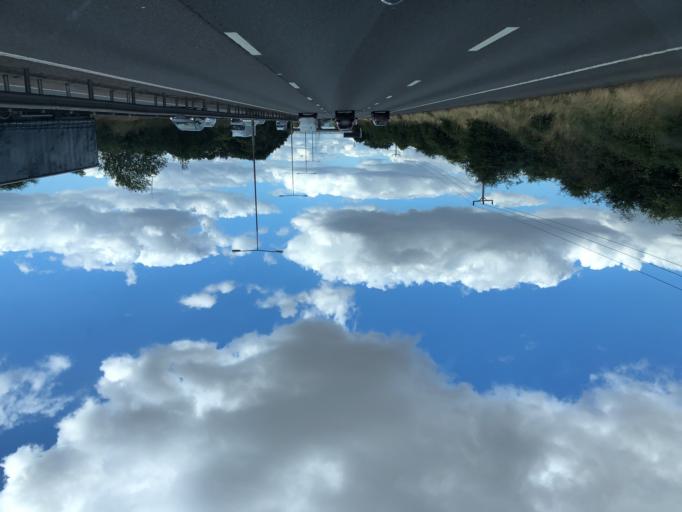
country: GB
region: England
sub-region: Northamptonshire
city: Hartwell
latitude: 52.1702
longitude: -0.8671
